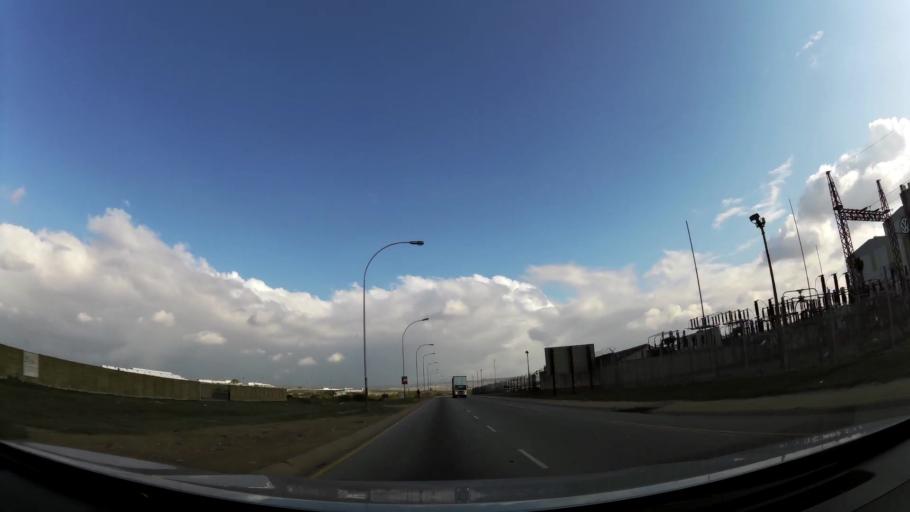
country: ZA
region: Eastern Cape
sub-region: Nelson Mandela Bay Metropolitan Municipality
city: Uitenhage
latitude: -33.7874
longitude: 25.4237
